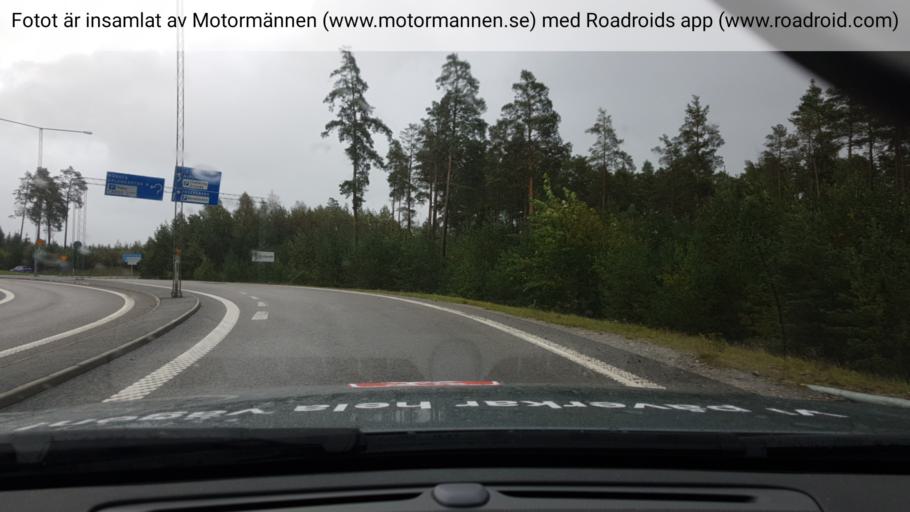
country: SE
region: Stockholm
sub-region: Sigtuna Kommun
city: Rosersberg
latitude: 59.6267
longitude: 17.9221
